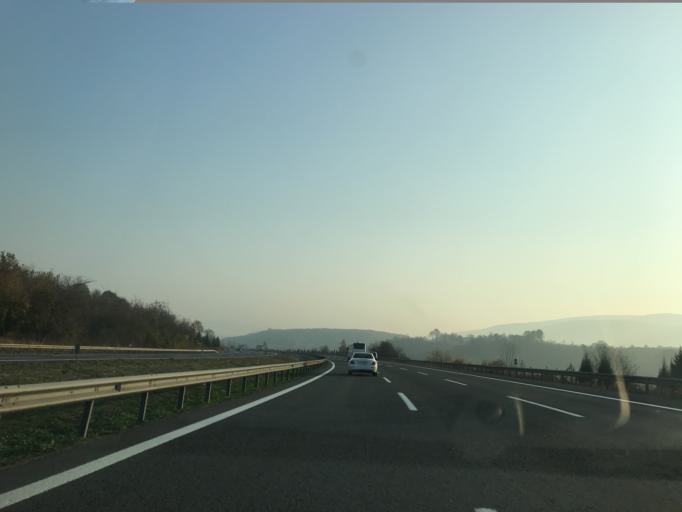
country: TR
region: Sakarya
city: Hendek
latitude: 40.7698
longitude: 30.7775
